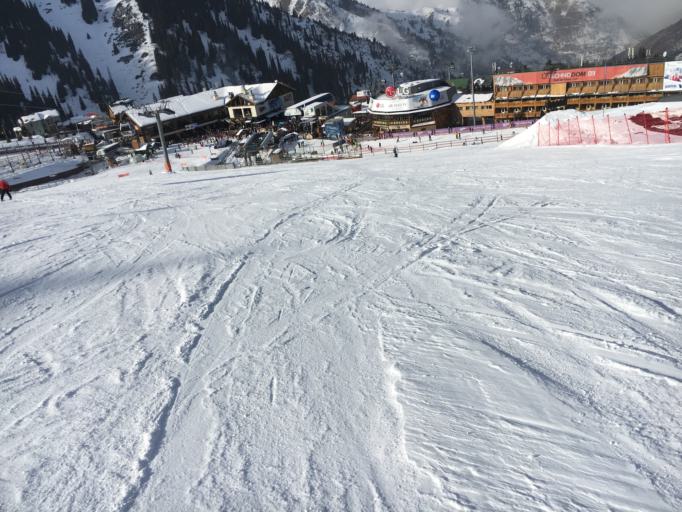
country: KZ
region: Almaty Qalasy
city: Almaty
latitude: 43.1270
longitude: 77.0835
